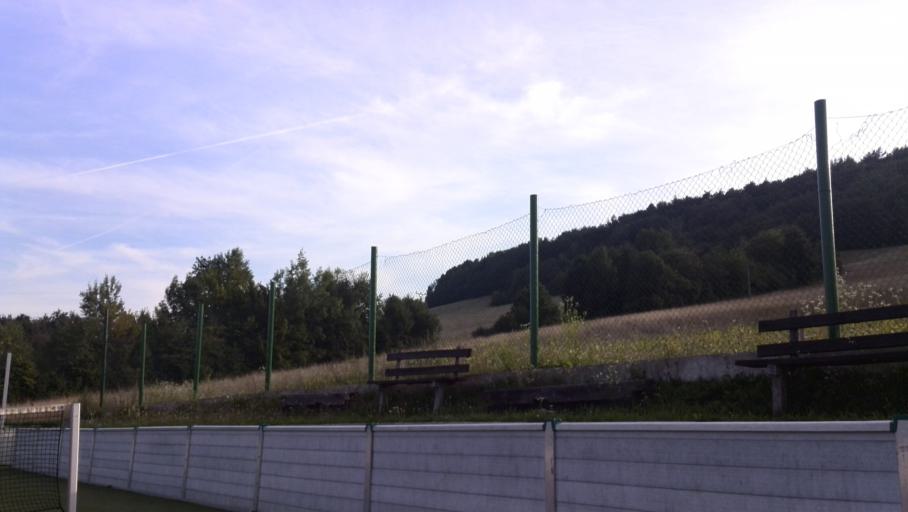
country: SK
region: Presovsky
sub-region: Okres Presov
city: Presov
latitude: 48.9366
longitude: 21.1760
